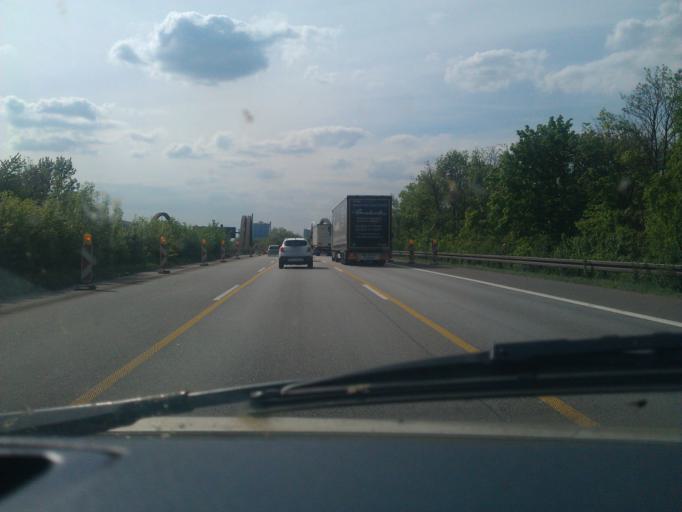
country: DE
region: North Rhine-Westphalia
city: Meiderich
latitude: 51.4865
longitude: 6.7608
